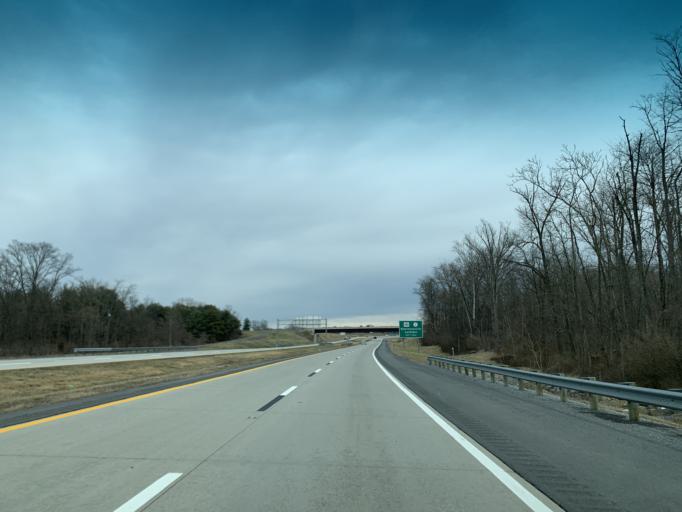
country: US
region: West Virginia
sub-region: Berkeley County
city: Martinsburg
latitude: 39.3939
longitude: -77.9044
